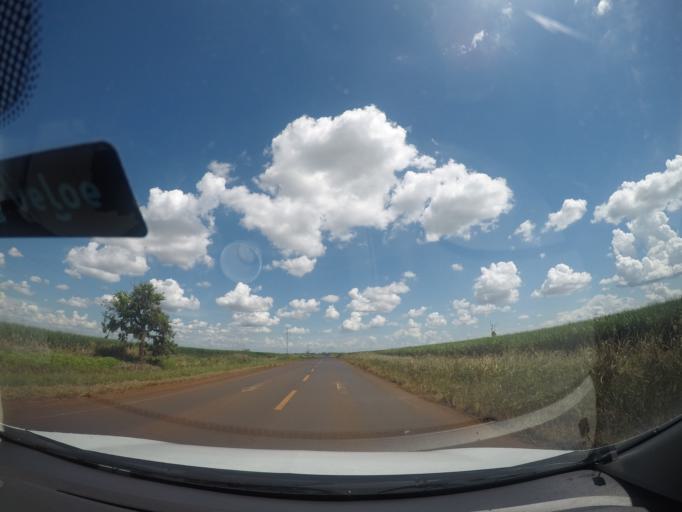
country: BR
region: Minas Gerais
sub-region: Frutal
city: Frutal
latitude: -19.8229
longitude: -48.7324
